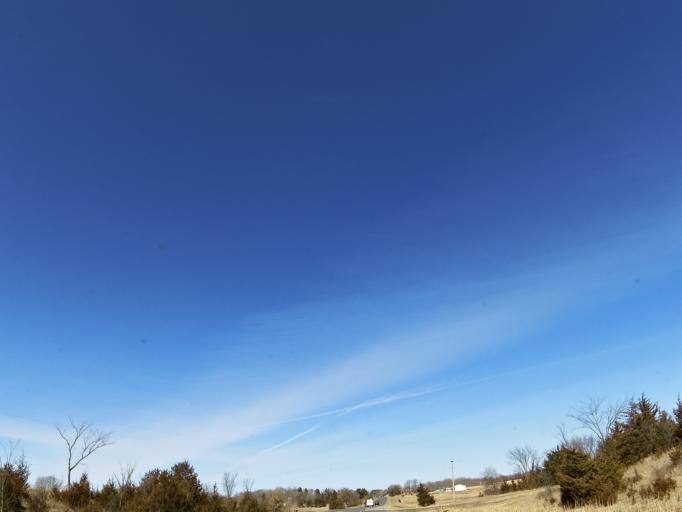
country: US
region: Minnesota
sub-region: Wright County
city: Rockford
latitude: 45.1018
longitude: -93.7758
